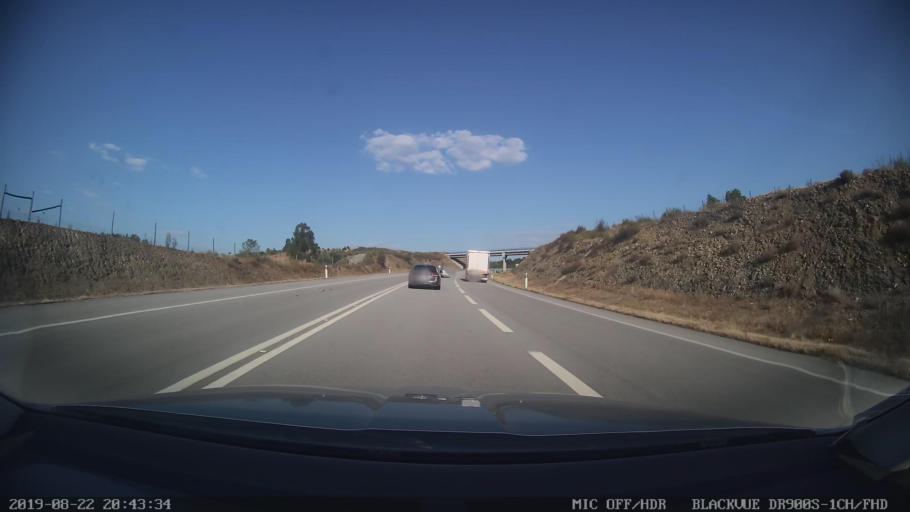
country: PT
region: Castelo Branco
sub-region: Proenca-A-Nova
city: Proenca-a-Nova
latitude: 39.6999
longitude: -7.8341
